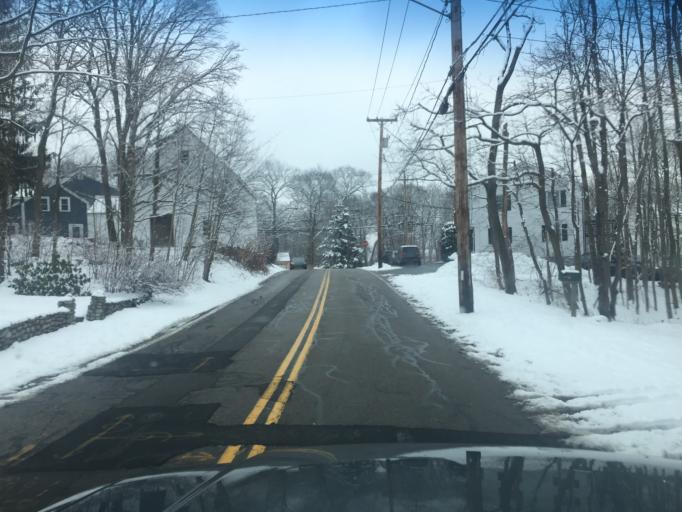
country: US
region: Massachusetts
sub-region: Norfolk County
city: Westwood
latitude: 42.2213
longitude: -71.2244
